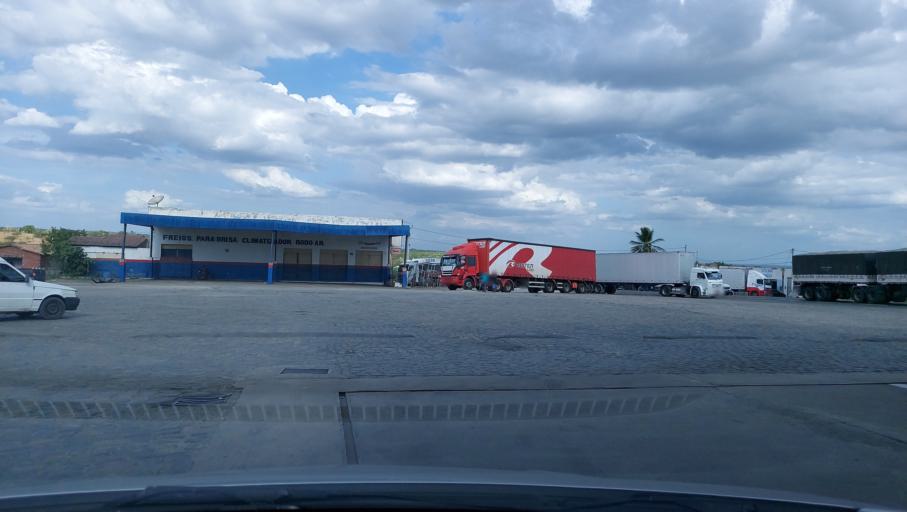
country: BR
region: Bahia
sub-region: Castro Alves
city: Castro Alves
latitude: -12.5811
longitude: -39.5180
